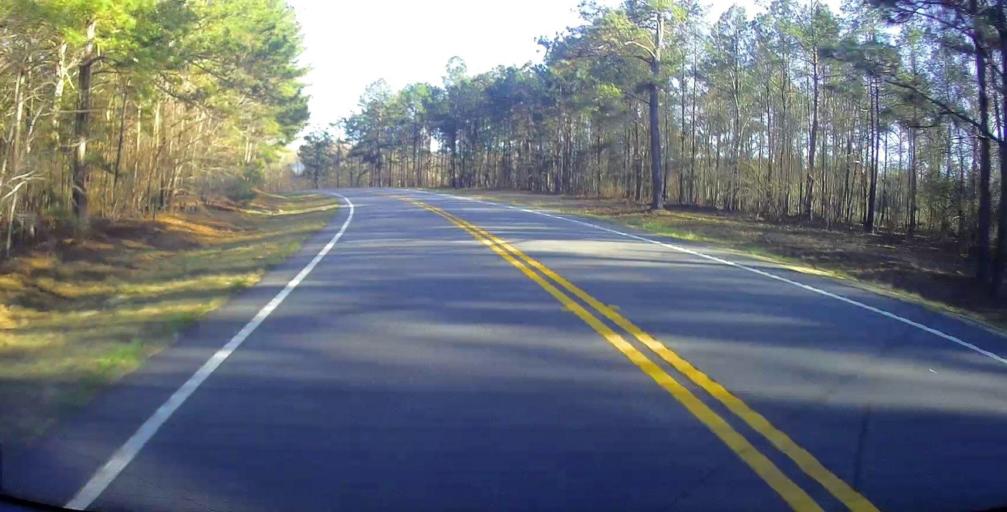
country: US
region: Georgia
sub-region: Taylor County
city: Butler
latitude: 32.4828
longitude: -84.3971
